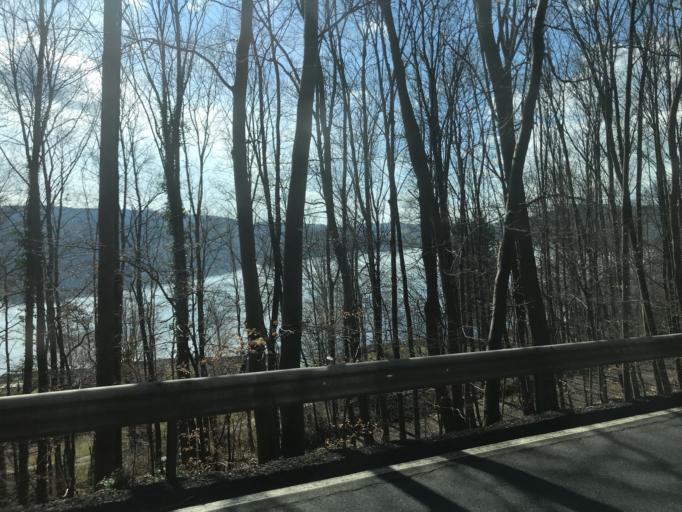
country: DE
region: Rheinland-Pfalz
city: Glees
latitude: 50.4232
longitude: 7.2659
